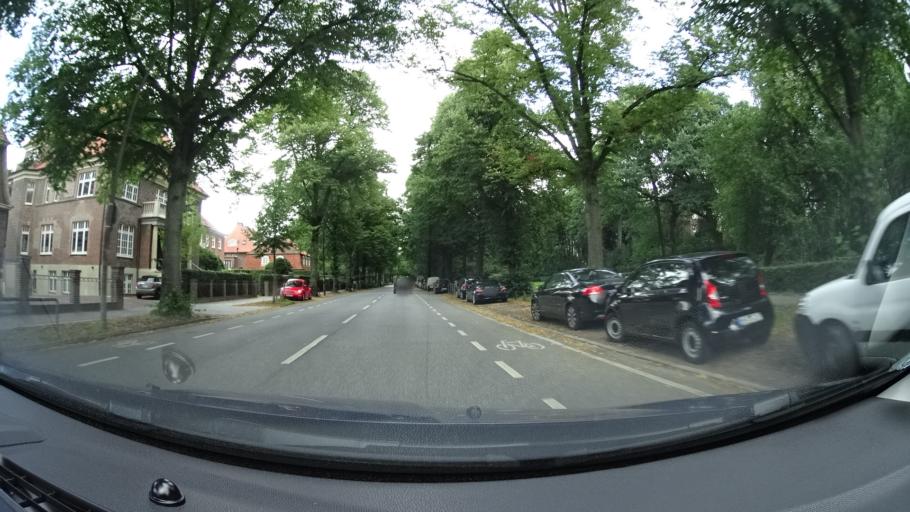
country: DE
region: Hamburg
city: Winterhude
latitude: 53.5959
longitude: 9.9949
